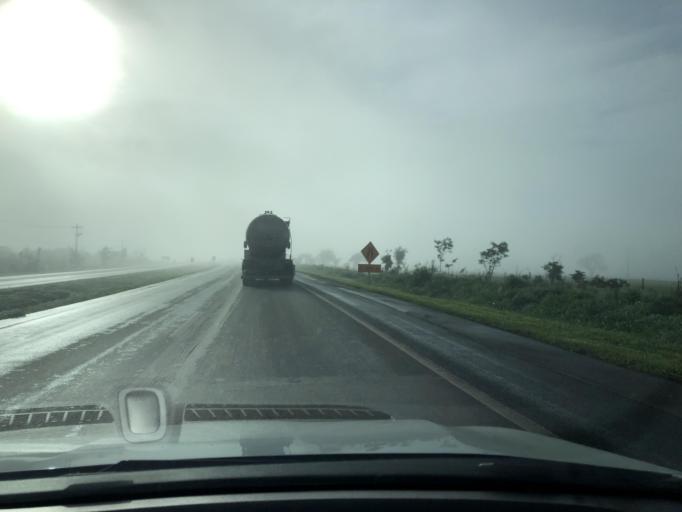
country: BR
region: Goias
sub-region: Luziania
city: Luziania
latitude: -16.2656
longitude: -47.8893
